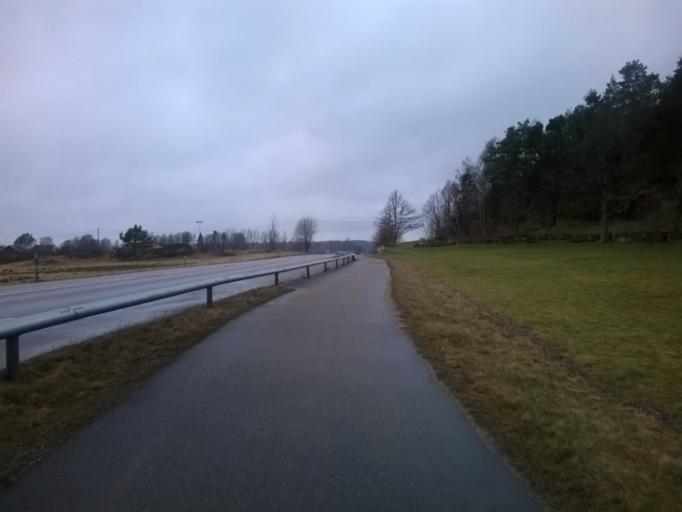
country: SE
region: Vaestra Goetaland
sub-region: Kungalvs Kommun
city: Kungalv
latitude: 57.8987
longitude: 11.9327
